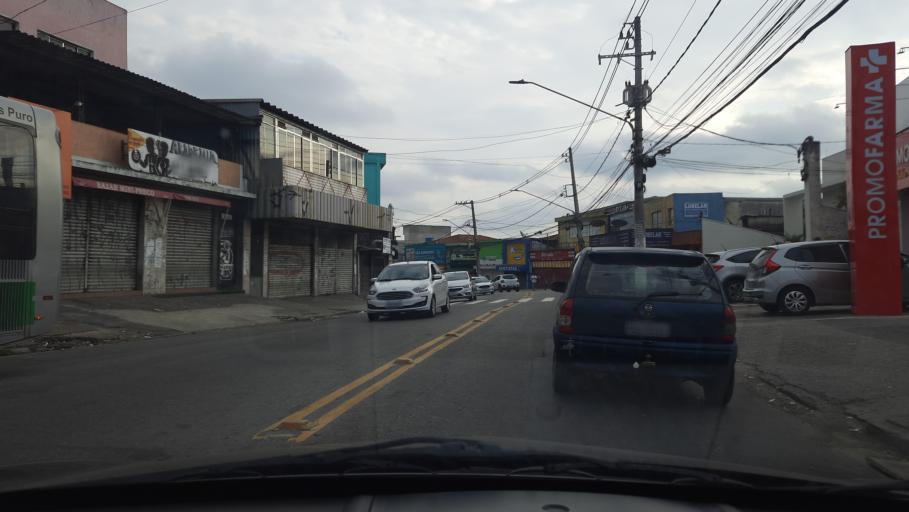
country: BR
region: Sao Paulo
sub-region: Caieiras
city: Caieiras
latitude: -23.4496
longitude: -46.7349
